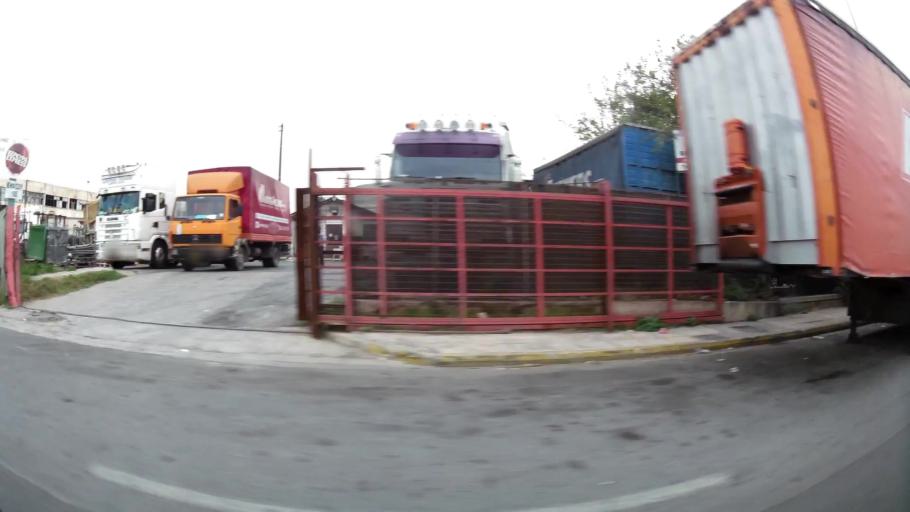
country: GR
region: Attica
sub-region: Nomarchia Athinas
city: Aigaleo
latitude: 37.9789
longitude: 23.6803
